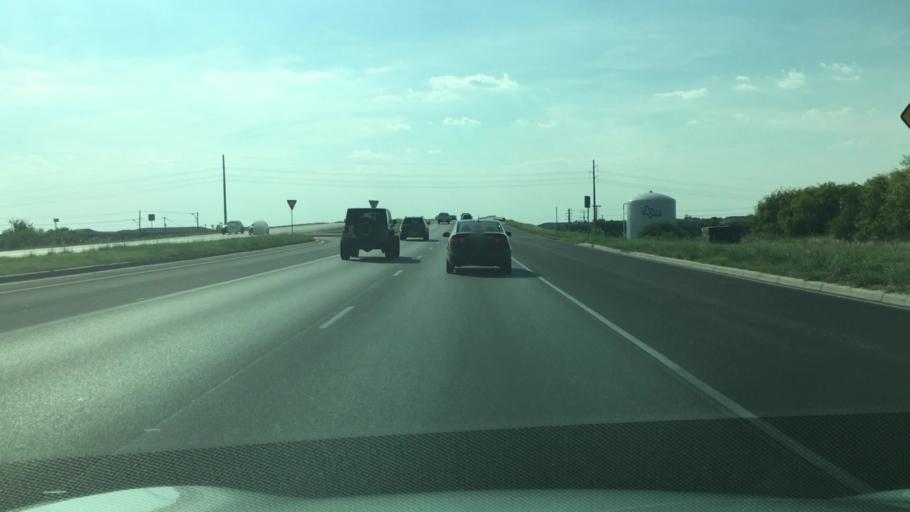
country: US
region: Texas
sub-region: Hays County
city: Kyle
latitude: 30.0159
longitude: -97.8662
